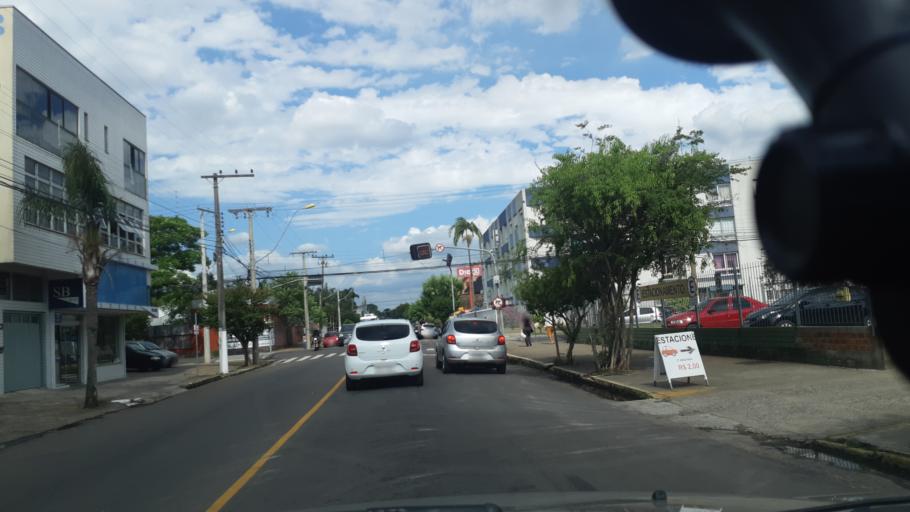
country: BR
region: Rio Grande do Sul
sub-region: Esteio
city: Esteio
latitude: -29.8503
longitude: -51.1740
